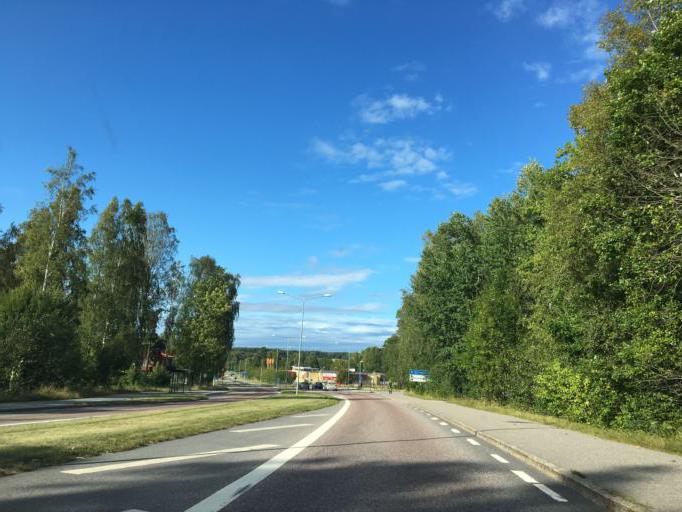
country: SE
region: Soedermanland
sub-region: Nykopings Kommun
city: Nykoping
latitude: 58.7660
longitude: 16.9886
